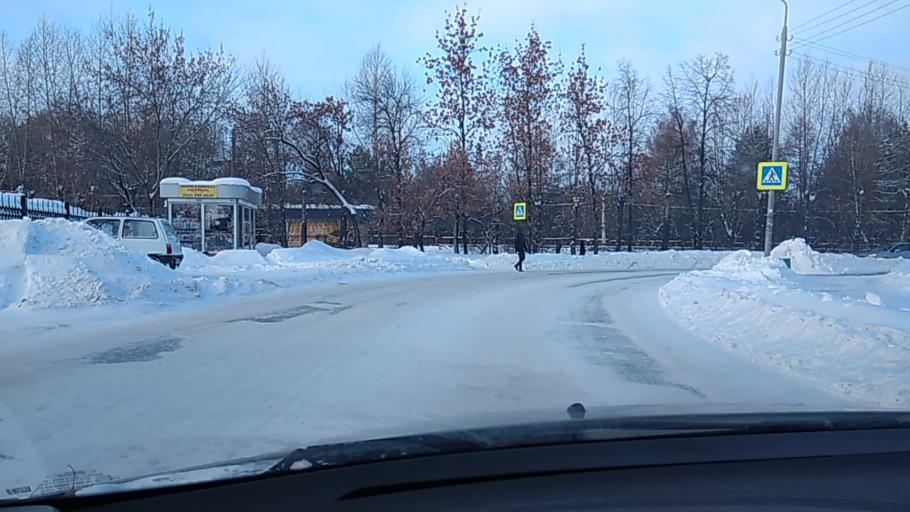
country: RU
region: Sverdlovsk
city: Yekaterinburg
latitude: 56.7928
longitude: 60.6077
